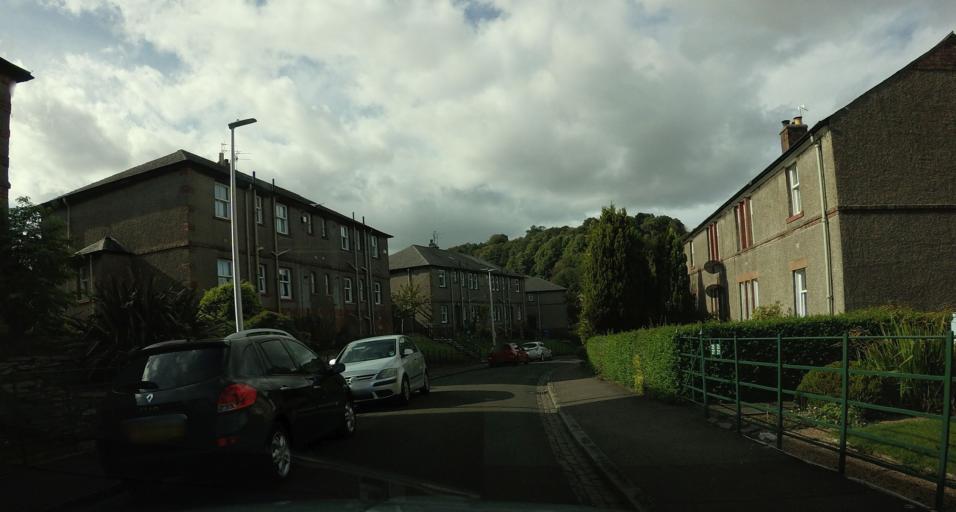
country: GB
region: Scotland
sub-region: Dundee City
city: Dundee
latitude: 56.4615
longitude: -3.0026
